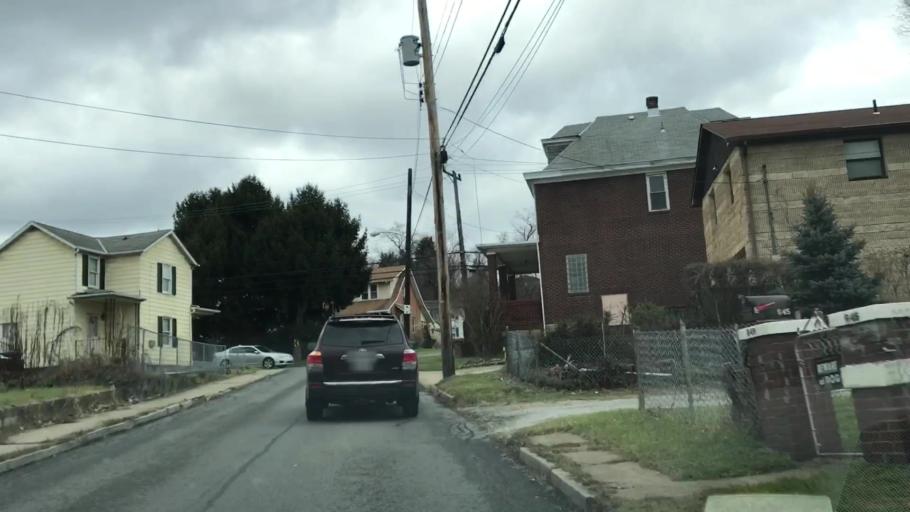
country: US
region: Pennsylvania
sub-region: Allegheny County
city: Heidelberg
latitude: 40.4043
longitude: -80.0974
